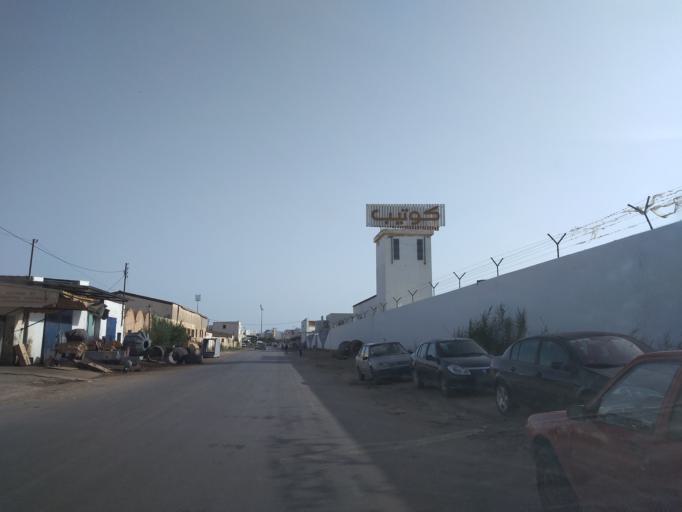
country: TN
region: Safaqis
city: Sfax
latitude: 34.7282
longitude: 10.7464
